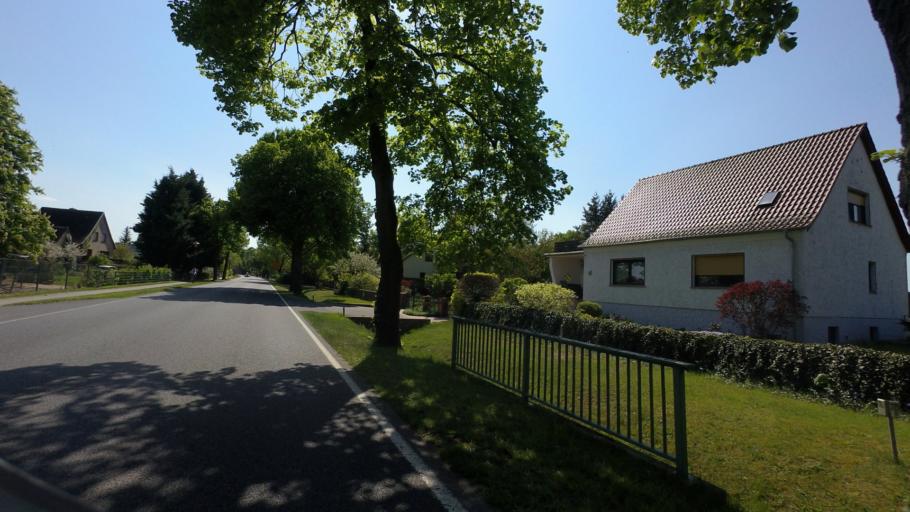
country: DE
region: Brandenburg
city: Tauche
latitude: 52.1210
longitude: 14.1929
